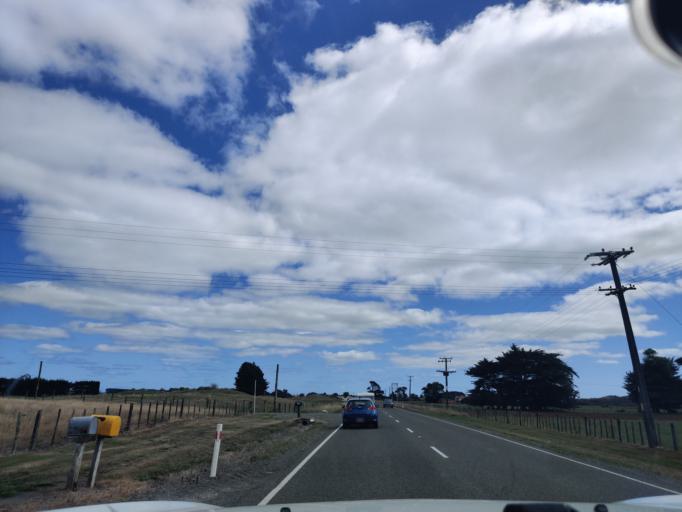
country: NZ
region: Manawatu-Wanganui
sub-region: Horowhenua District
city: Foxton
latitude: -40.4184
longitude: 175.4087
